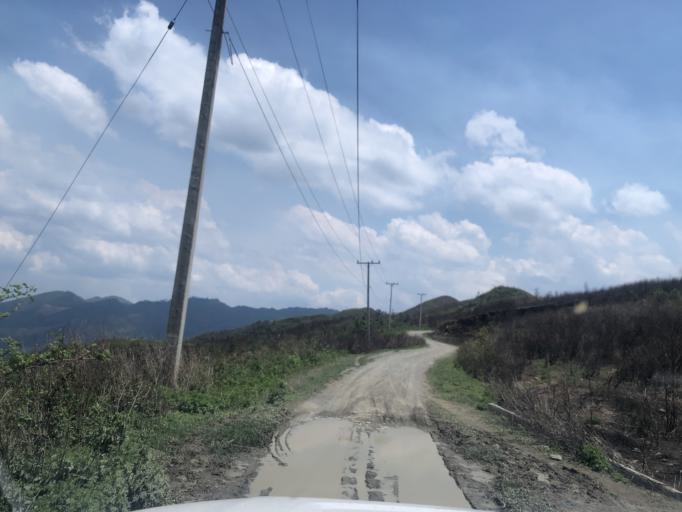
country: LA
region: Phongsali
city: Phongsali
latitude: 21.4174
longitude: 102.1849
